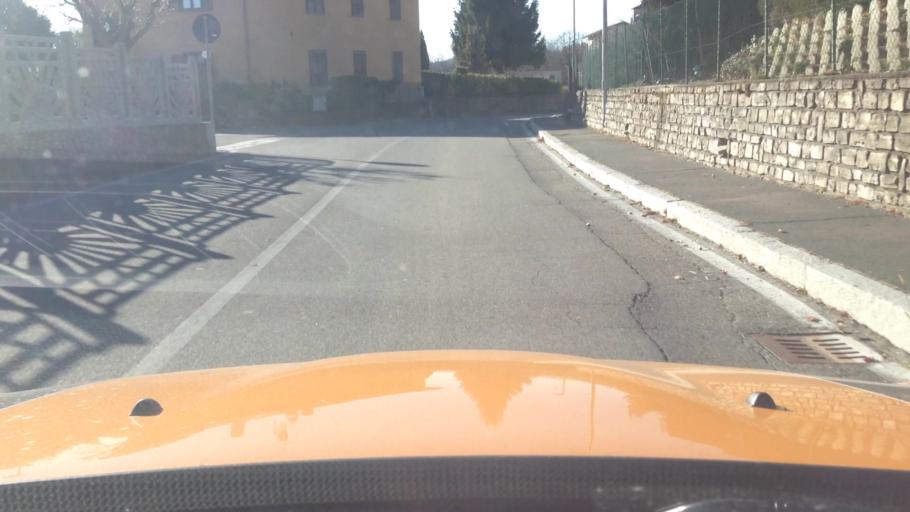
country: IT
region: Lombardy
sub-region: Provincia di Como
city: Bizzarone
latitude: 45.8340
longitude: 8.9397
